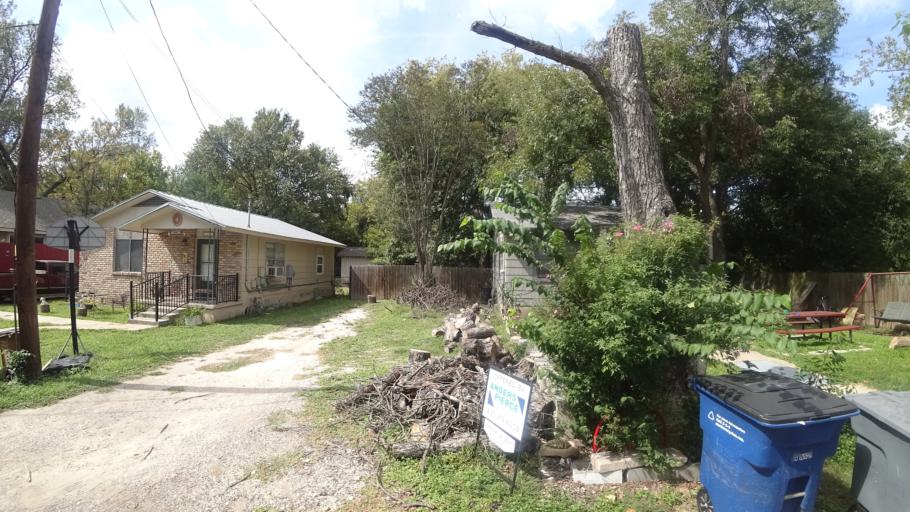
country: US
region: Texas
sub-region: Travis County
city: Austin
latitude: 30.2676
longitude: -97.6991
